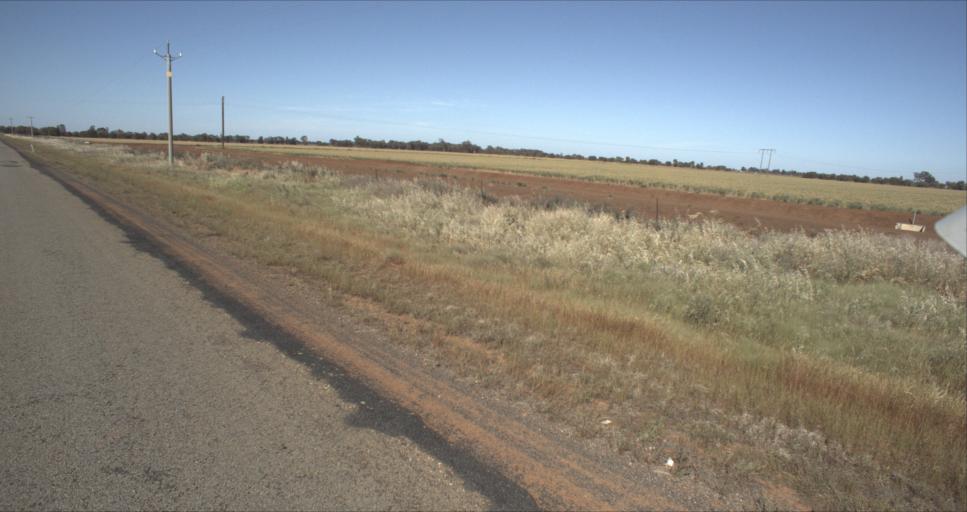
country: AU
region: New South Wales
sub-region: Leeton
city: Leeton
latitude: -34.5581
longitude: 146.2659
